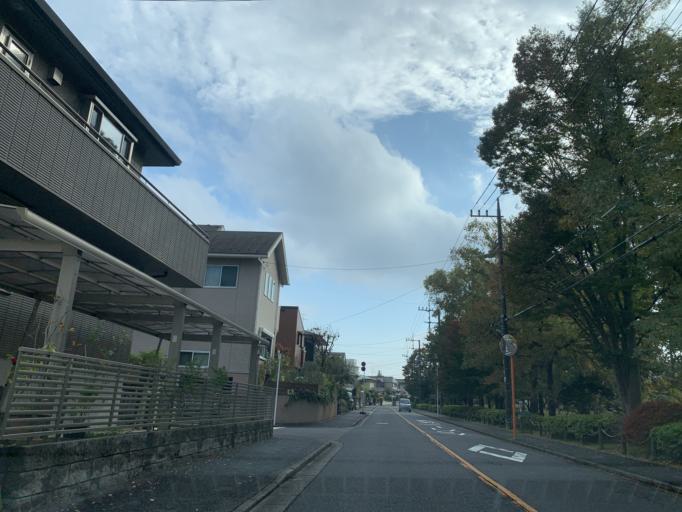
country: JP
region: Chiba
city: Nagareyama
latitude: 35.9051
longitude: 139.9142
